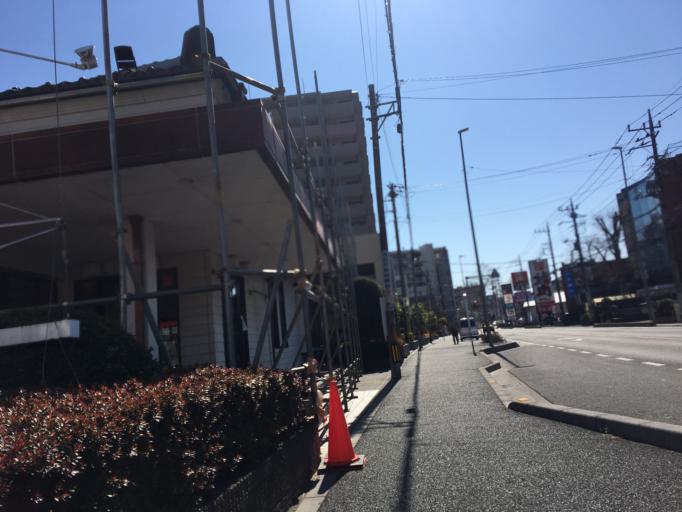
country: JP
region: Saitama
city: Shiki
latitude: 35.8138
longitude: 139.5766
